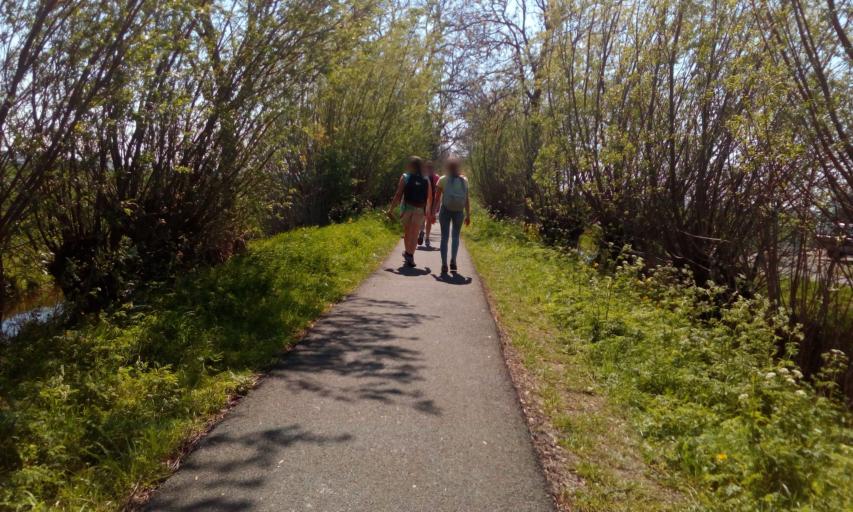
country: NL
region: South Holland
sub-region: Bodegraven-Reeuwijk
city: Bodegraven
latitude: 52.0923
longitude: 4.7093
